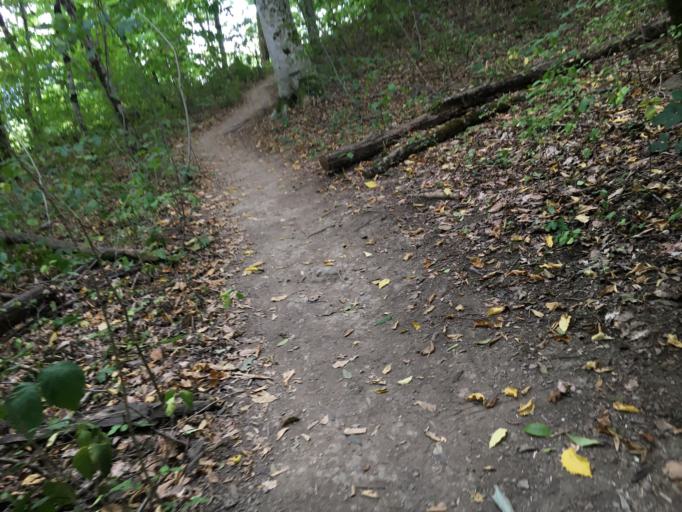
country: RU
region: Krasnodarskiy
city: Tuapse
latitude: 44.2531
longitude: 39.2285
